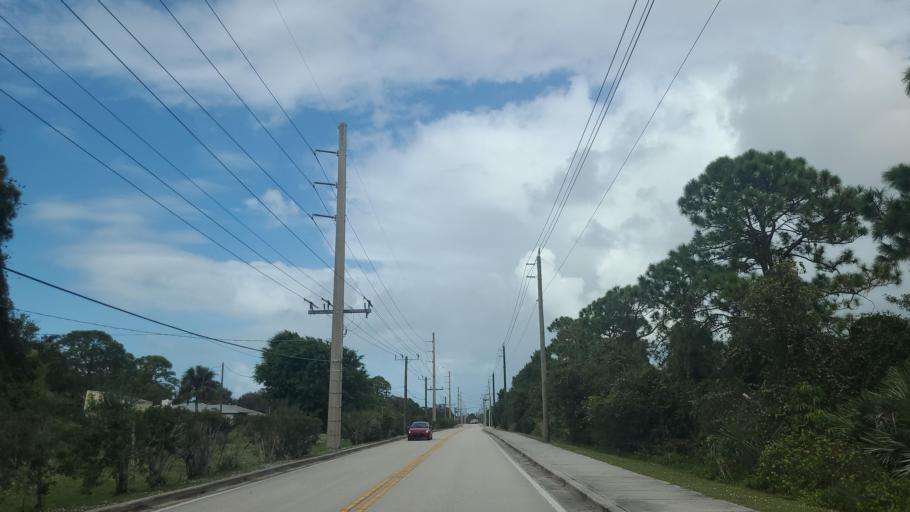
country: US
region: Florida
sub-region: Indian River County
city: Sebastian
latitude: 27.8087
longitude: -80.4781
